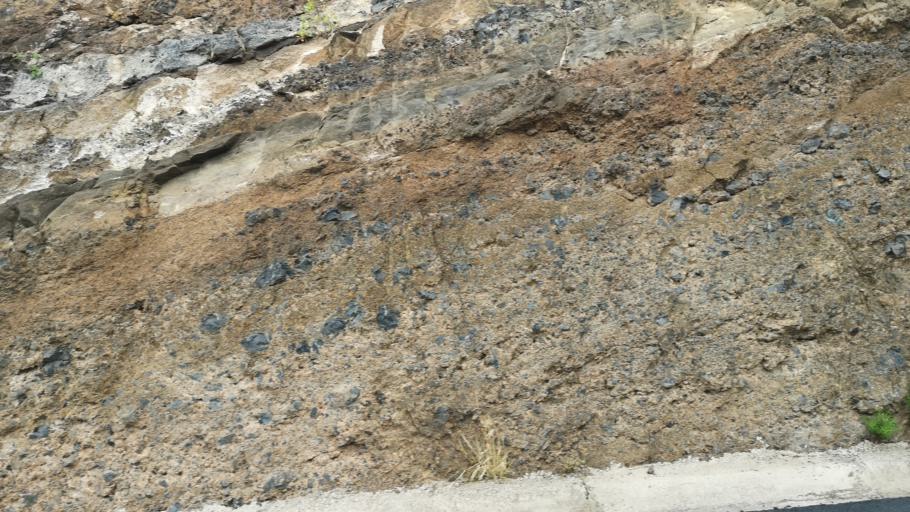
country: ES
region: Canary Islands
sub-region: Provincia de Santa Cruz de Tenerife
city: Alajero
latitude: 28.0569
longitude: -17.2018
